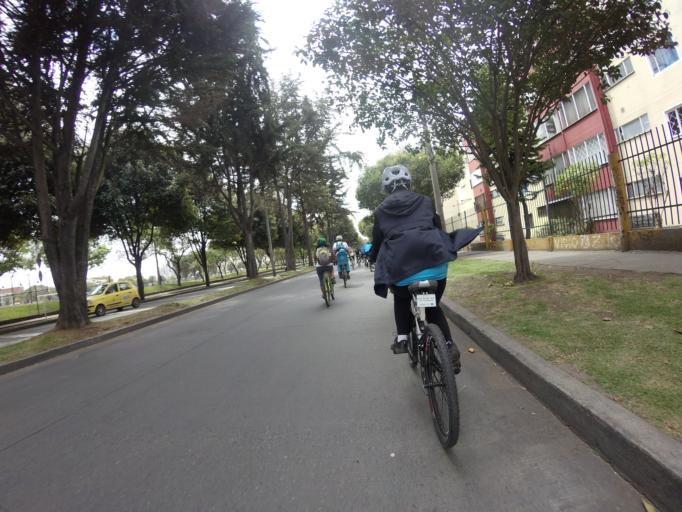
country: CO
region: Cundinamarca
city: Cota
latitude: 4.7141
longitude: -74.1112
